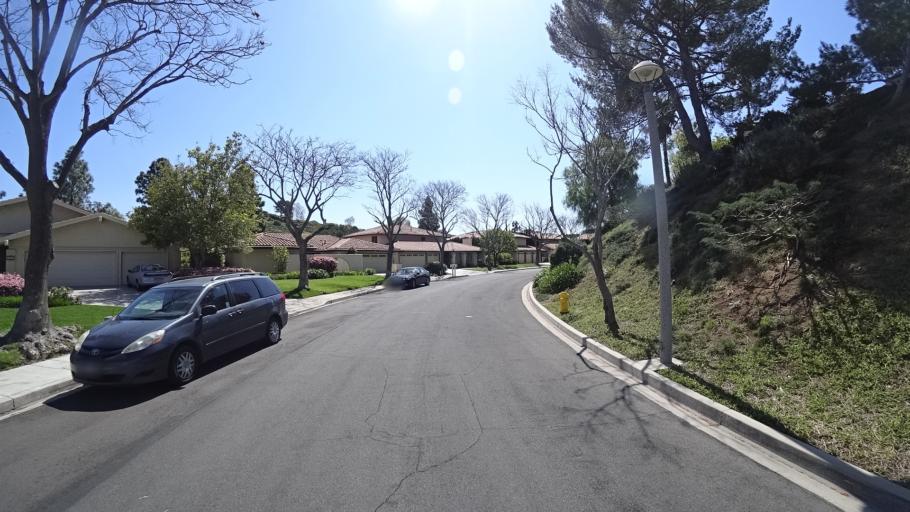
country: US
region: California
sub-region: Ventura County
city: Moorpark
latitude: 34.2350
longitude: -118.8531
